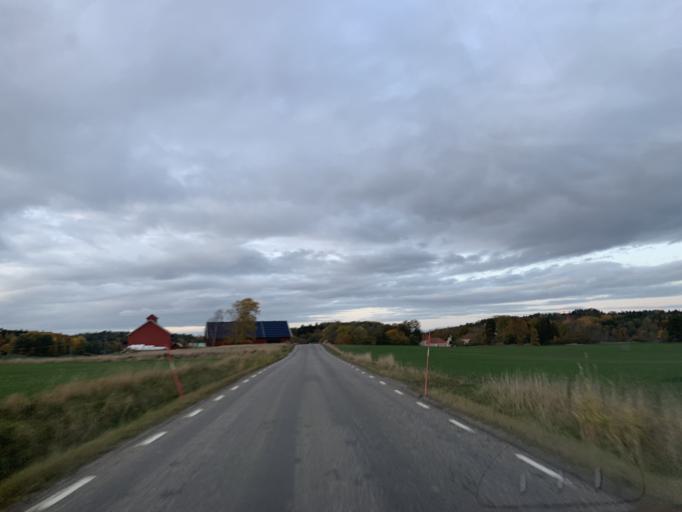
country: SE
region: Stockholm
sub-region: Nynashamns Kommun
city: Osmo
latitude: 58.9544
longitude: 17.7668
